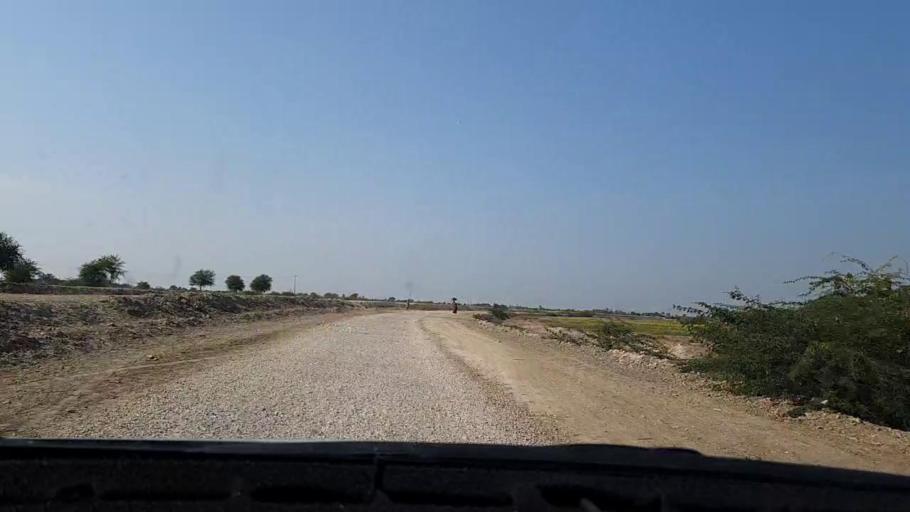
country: PK
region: Sindh
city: Tando Mittha Khan
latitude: 25.8192
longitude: 69.2965
